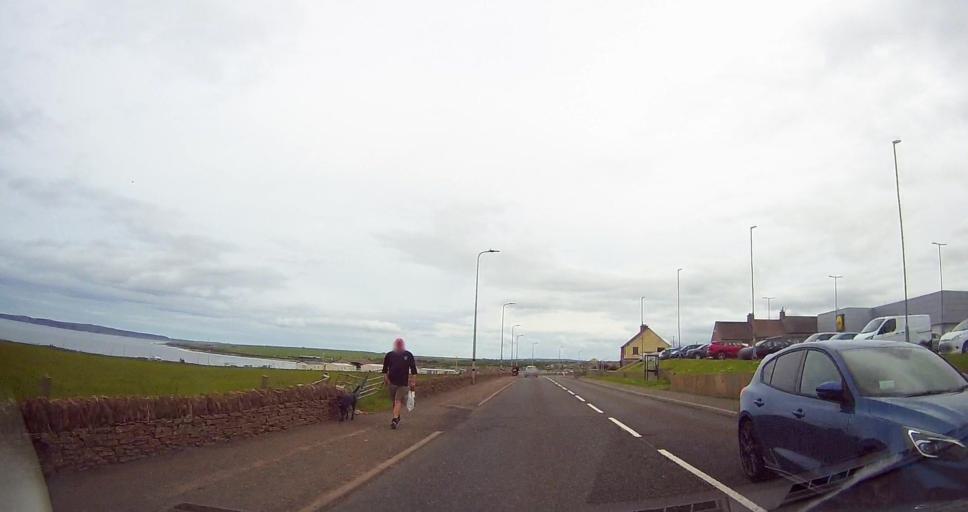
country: GB
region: Scotland
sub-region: Highland
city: Thurso
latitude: 58.5981
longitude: -3.5328
